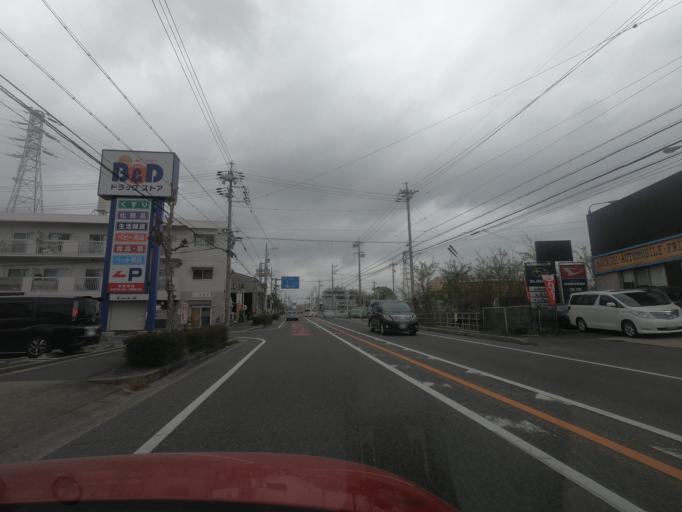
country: JP
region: Aichi
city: Kasugai
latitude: 35.2661
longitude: 136.9625
